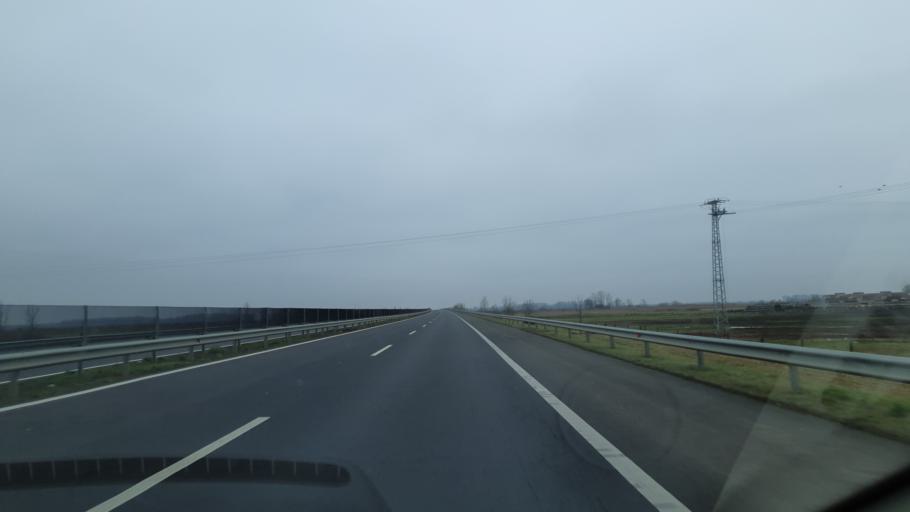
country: HU
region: Hajdu-Bihar
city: Hajdunanas
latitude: 47.8494
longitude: 21.3469
